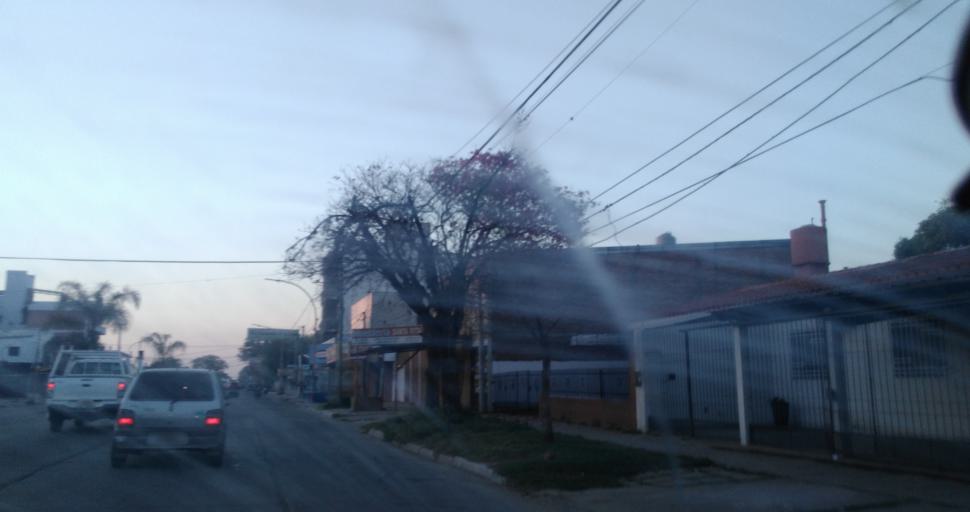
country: AR
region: Chaco
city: Resistencia
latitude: -27.4724
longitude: -58.9626
